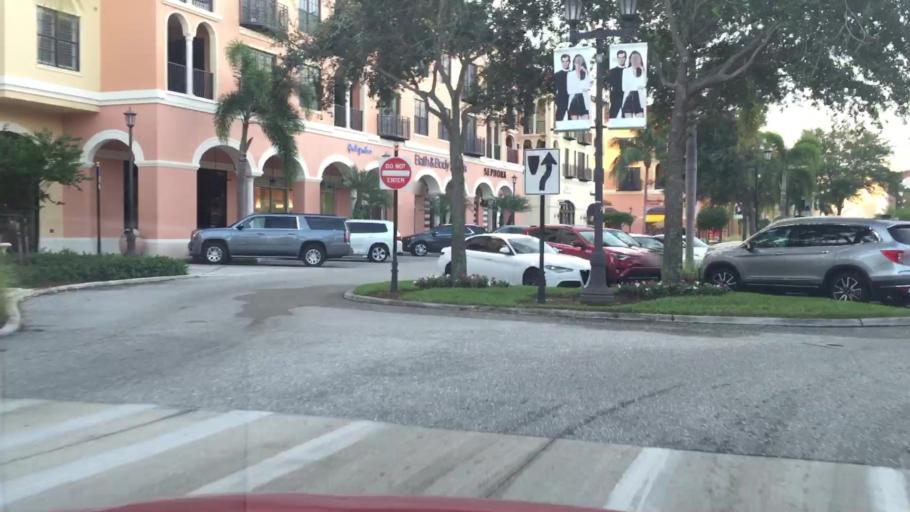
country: US
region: Florida
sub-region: Lee County
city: Estero
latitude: 26.4019
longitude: -81.8070
